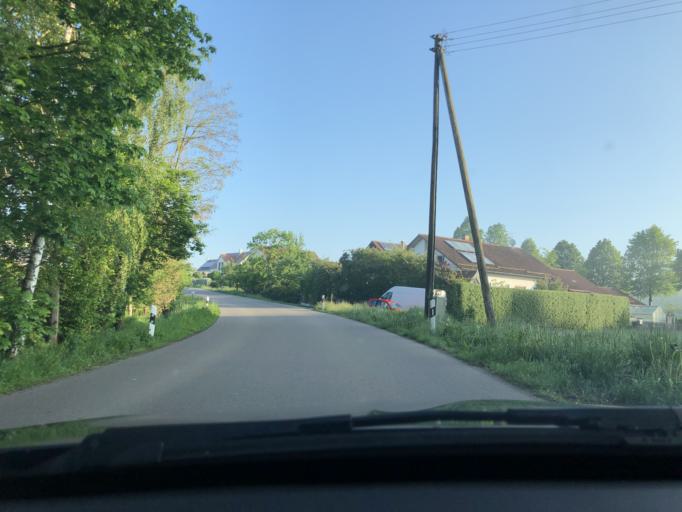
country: DE
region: Bavaria
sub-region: Upper Bavaria
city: Schweitenkirchen
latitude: 48.4899
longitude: 11.6219
